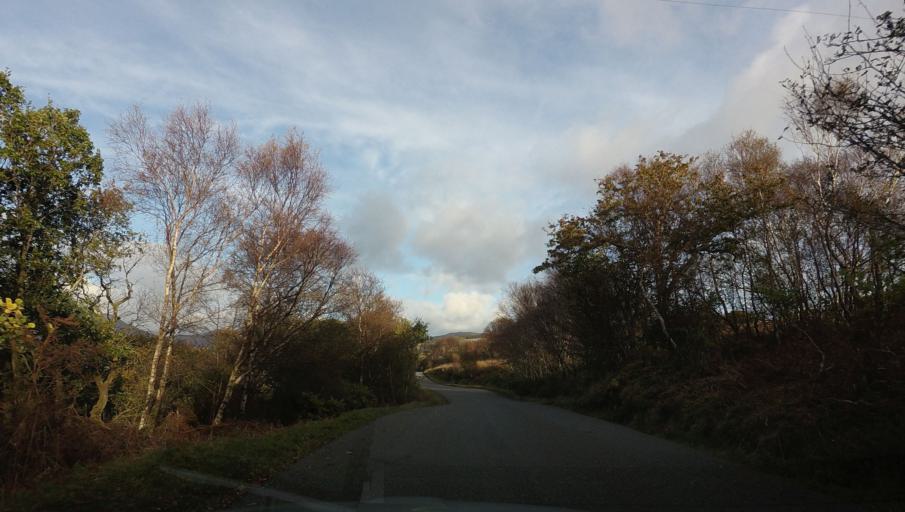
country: GB
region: Scotland
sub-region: Argyll and Bute
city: Isle Of Mull
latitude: 56.3627
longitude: -6.0345
